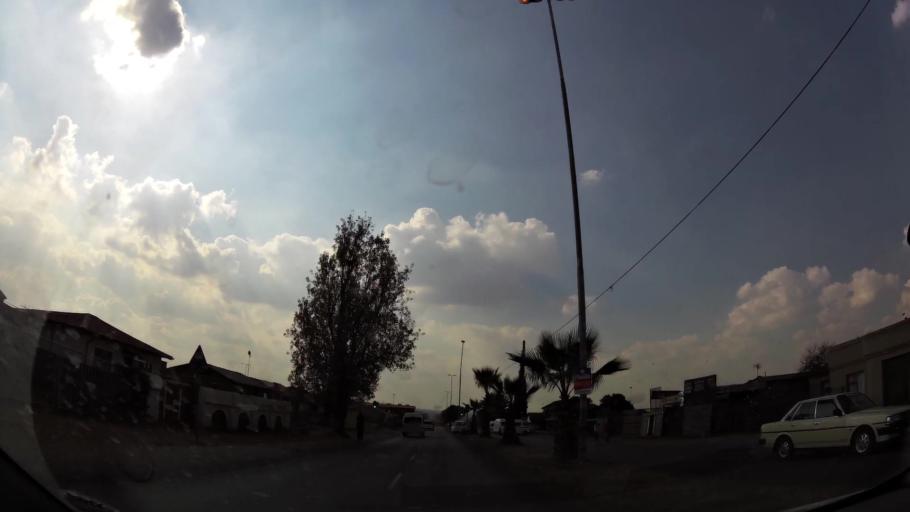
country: ZA
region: Gauteng
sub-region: Ekurhuleni Metropolitan Municipality
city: Germiston
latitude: -26.3163
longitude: 28.1511
